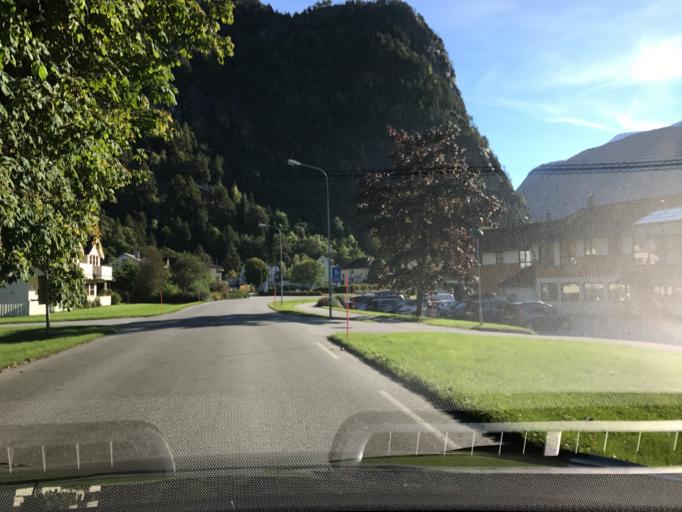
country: NO
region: More og Romsdal
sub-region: Norddal
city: Valldal
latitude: 62.3007
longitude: 7.2598
